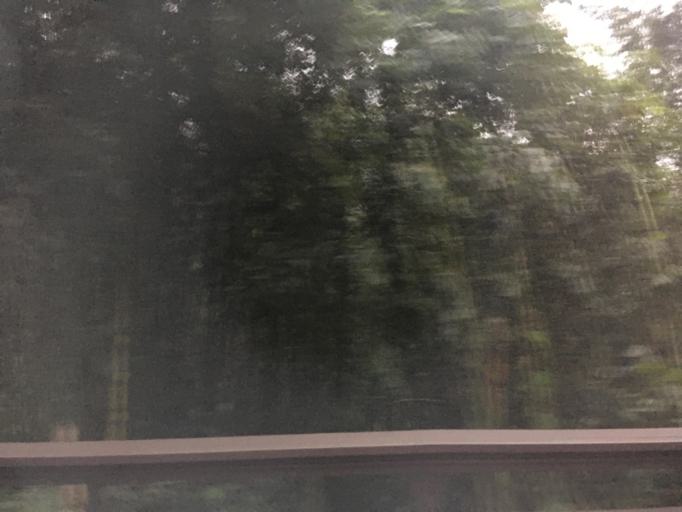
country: TW
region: Taiwan
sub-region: Chiayi
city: Jiayi Shi
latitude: 23.5056
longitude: 120.6604
